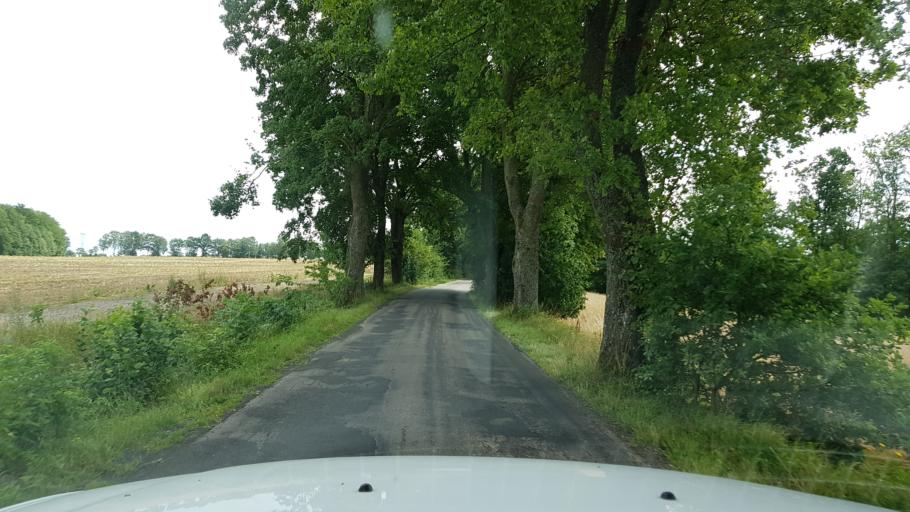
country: PL
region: West Pomeranian Voivodeship
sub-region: Powiat koszalinski
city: Mielno
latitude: 54.1599
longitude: 16.0727
